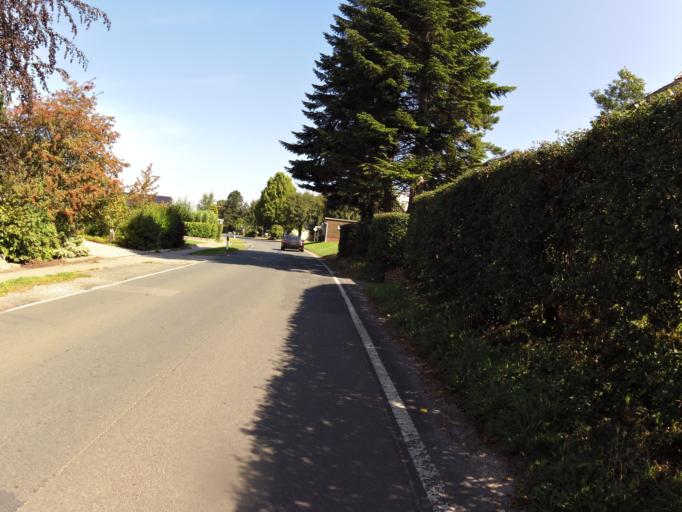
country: DE
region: Lower Saxony
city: Elsfleth
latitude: 53.2525
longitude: 8.4702
